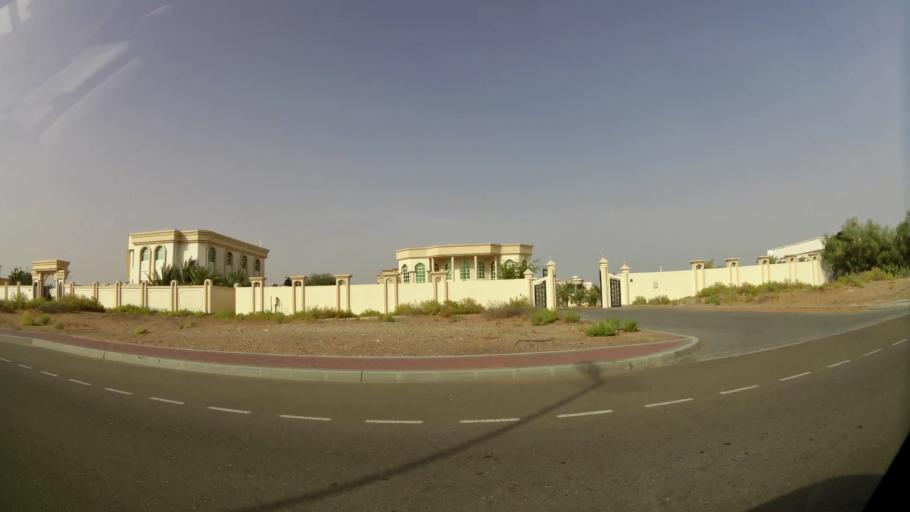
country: AE
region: Abu Dhabi
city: Al Ain
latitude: 24.2093
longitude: 55.6234
